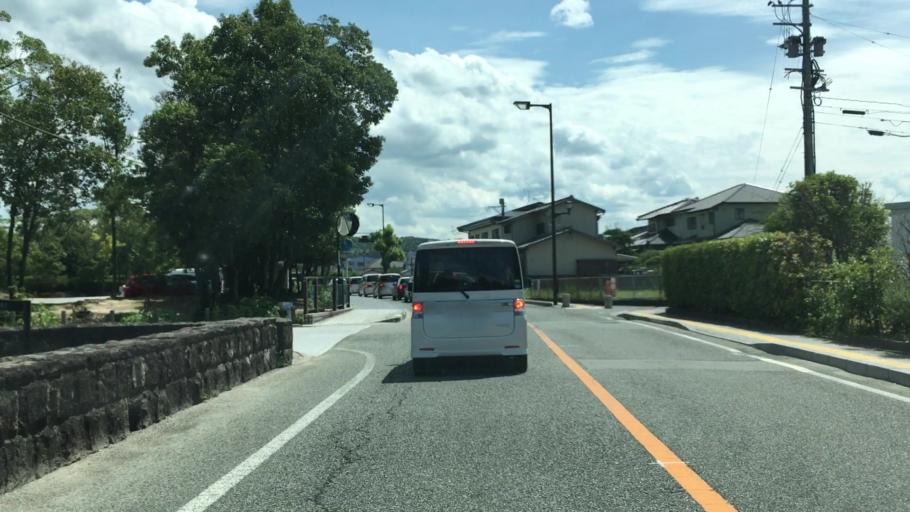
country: JP
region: Fukuoka
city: Dazaifu
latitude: 33.5133
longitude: 130.5139
